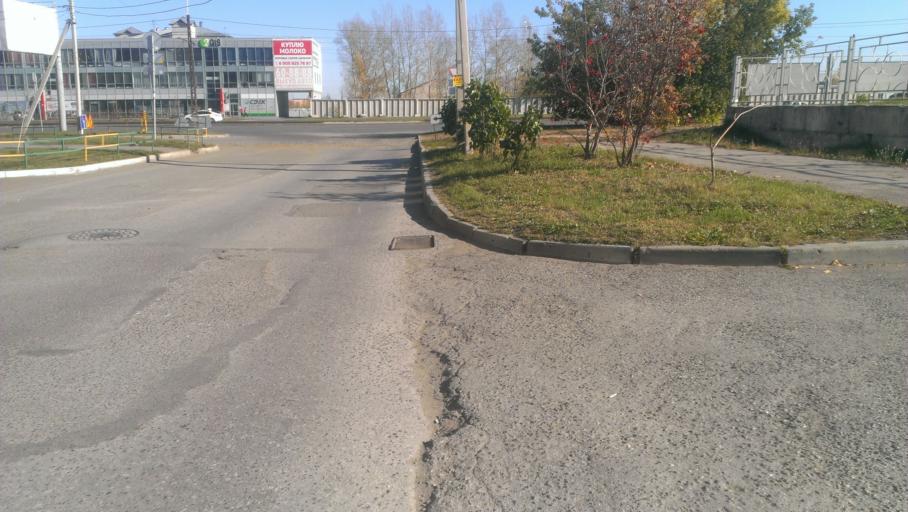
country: RU
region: Altai Krai
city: Novosilikatnyy
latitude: 53.3291
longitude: 83.6914
